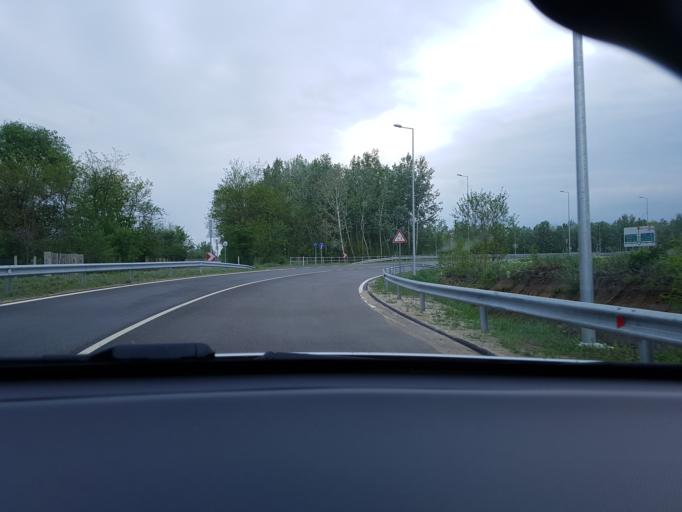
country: HU
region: Bacs-Kiskun
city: Kecskemet
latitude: 46.9325
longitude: 19.6322
